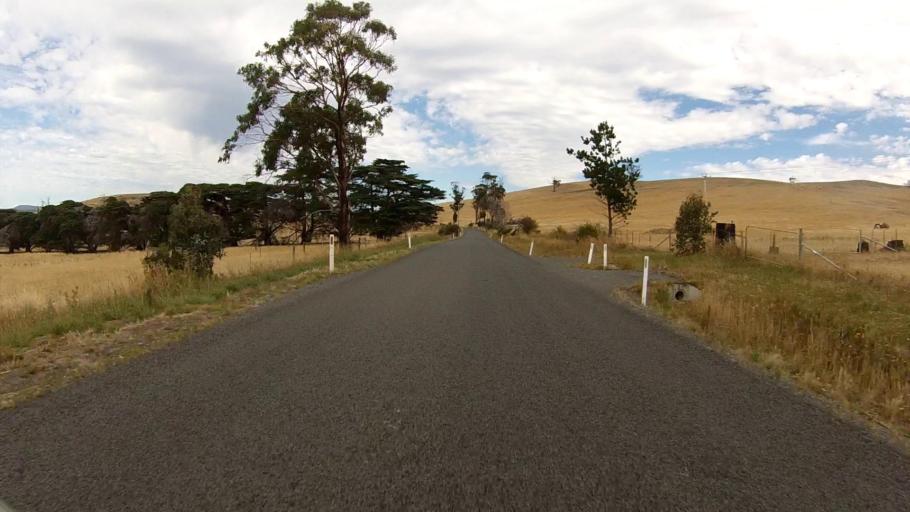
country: AU
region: Tasmania
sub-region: Sorell
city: Sorell
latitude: -42.8956
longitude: 147.7739
